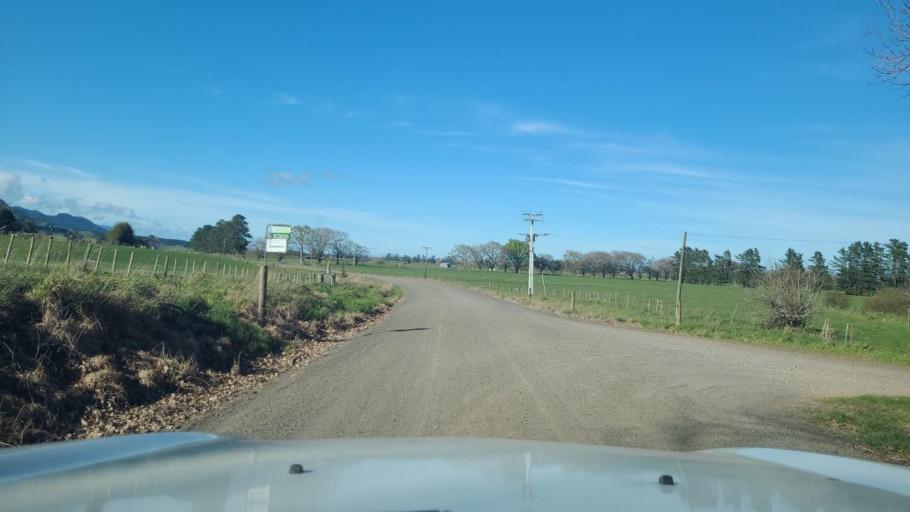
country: NZ
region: Bay of Plenty
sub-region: Western Bay of Plenty District
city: Katikati
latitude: -37.6132
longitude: 175.7957
